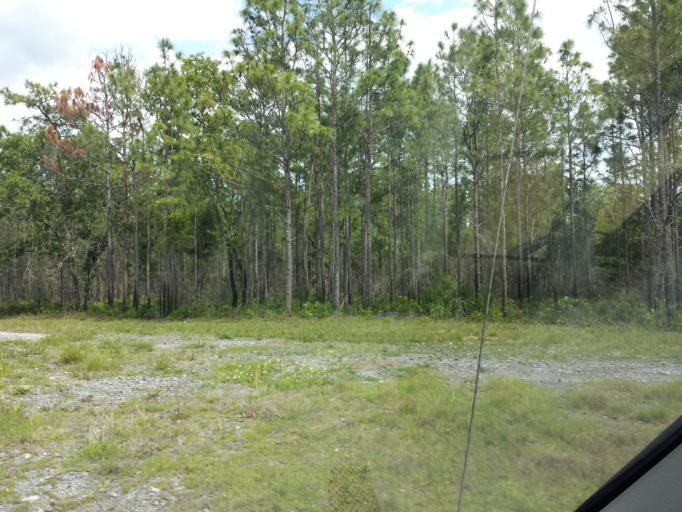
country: US
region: Florida
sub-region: Hernando County
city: Hill 'n Dale
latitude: 28.5366
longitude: -82.2664
